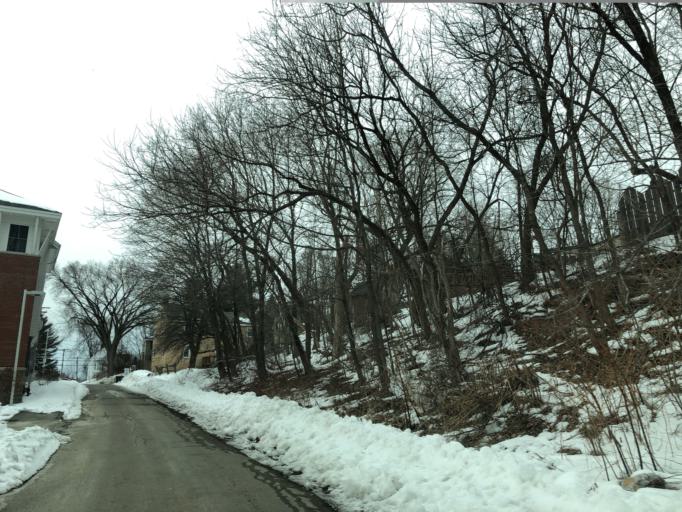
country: US
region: Maine
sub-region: Cumberland County
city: Westbrook
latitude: 43.6799
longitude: -70.3669
